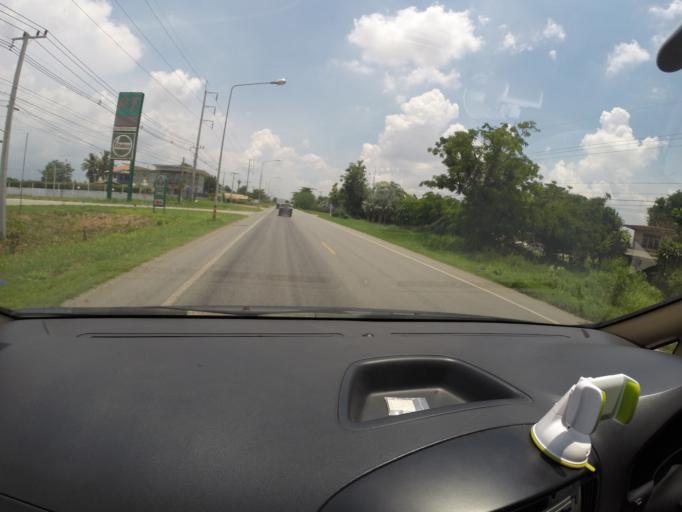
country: TH
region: Nakhon Ratchasima
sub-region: Amphoe Thepharak
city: Thepharak
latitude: 15.1226
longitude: 101.5199
